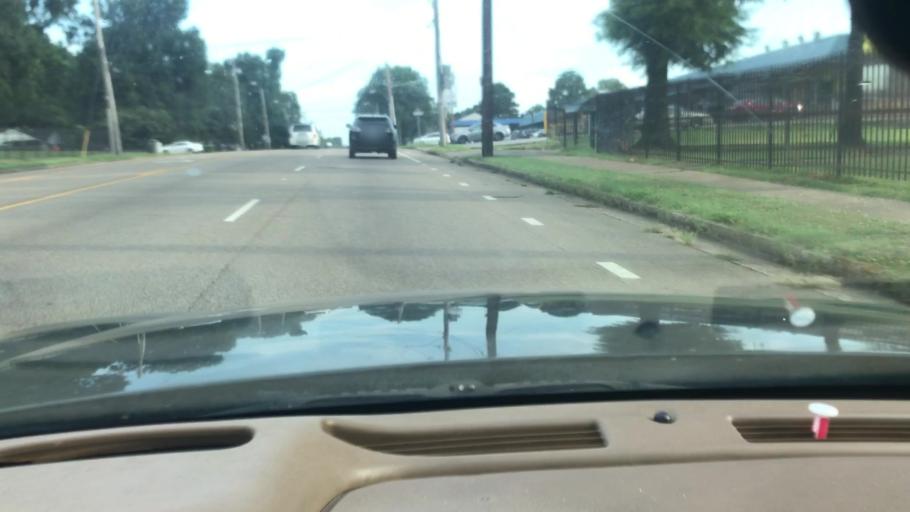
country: US
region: Mississippi
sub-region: De Soto County
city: Southaven
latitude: 35.0499
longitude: -90.0076
